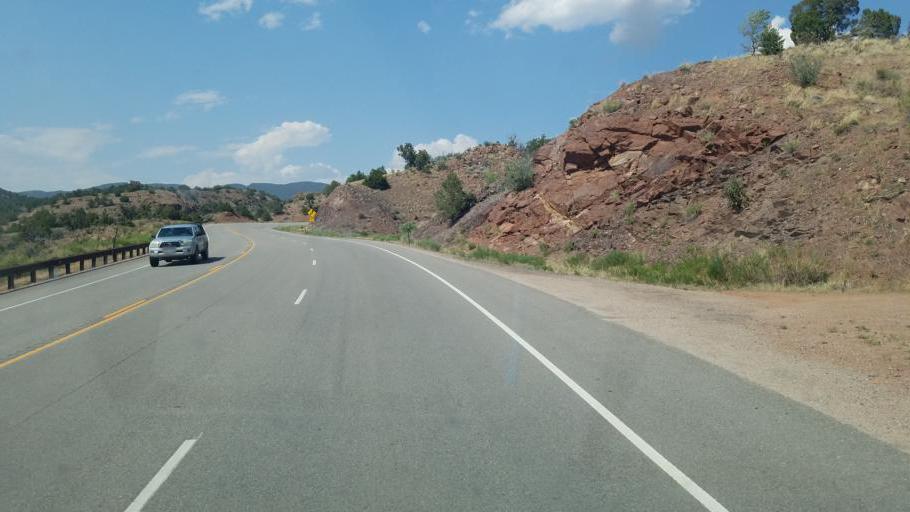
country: US
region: Colorado
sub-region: Fremont County
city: Canon City
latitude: 38.4923
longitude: -105.3637
